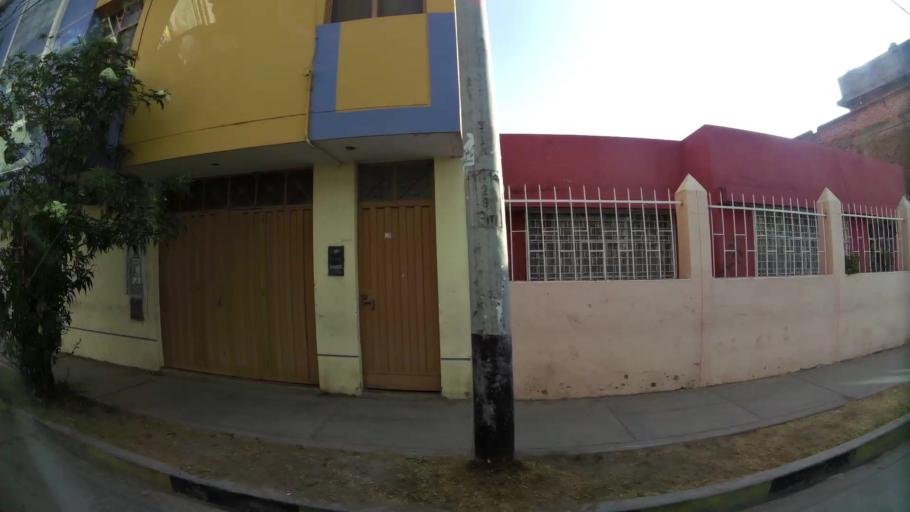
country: PE
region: Junin
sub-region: Provincia de Huancayo
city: El Tambo
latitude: -12.0529
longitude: -75.2190
